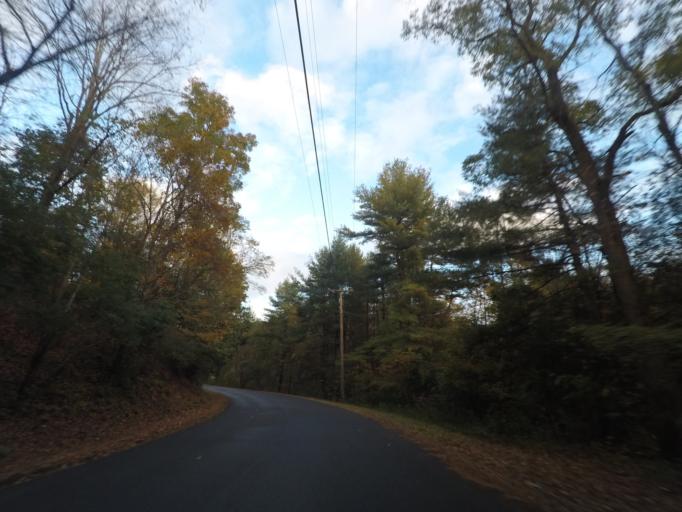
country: US
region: New York
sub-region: Rensselaer County
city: Nassau
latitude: 42.5523
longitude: -73.5932
